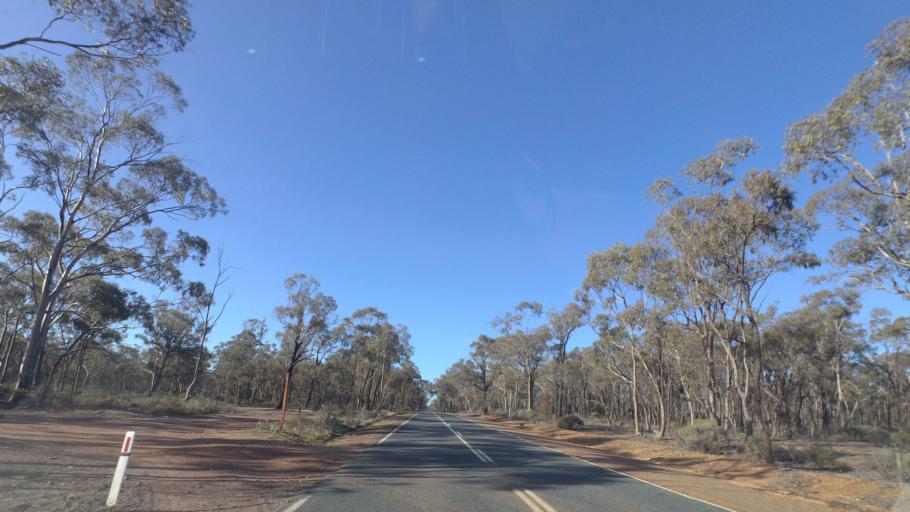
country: AU
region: Victoria
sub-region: Greater Bendigo
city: Epsom
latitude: -36.6692
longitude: 144.4228
